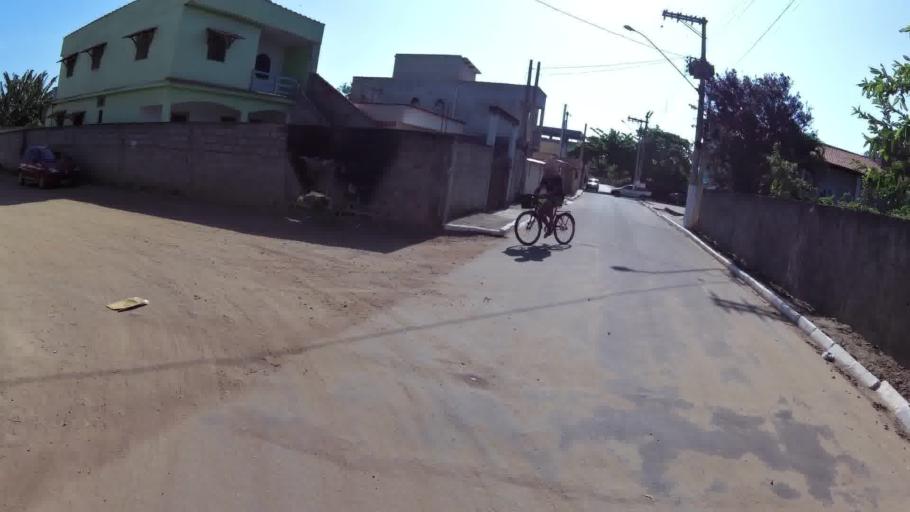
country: BR
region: Espirito Santo
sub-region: Piuma
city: Piuma
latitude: -20.8908
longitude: -40.7681
